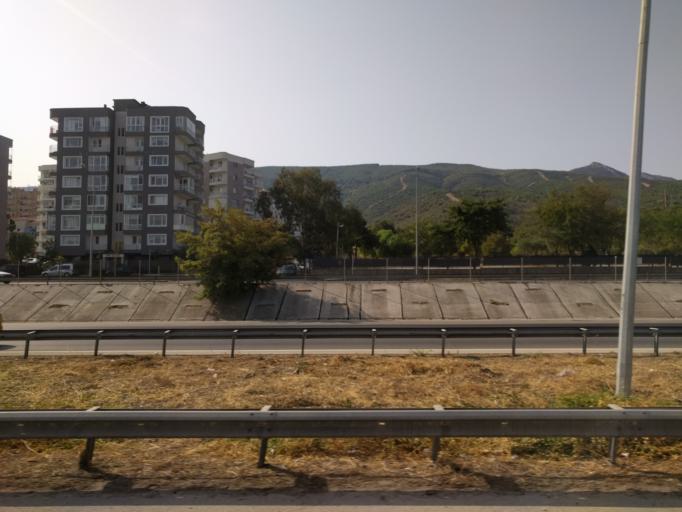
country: TR
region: Izmir
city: Karsiyaka
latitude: 38.3965
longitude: 26.9872
